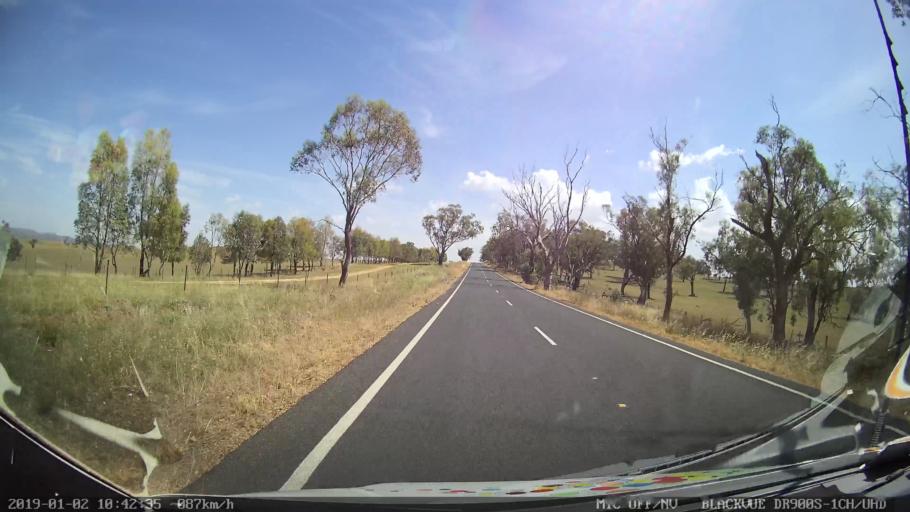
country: AU
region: New South Wales
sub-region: Cootamundra
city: Cootamundra
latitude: -34.7827
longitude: 148.3068
